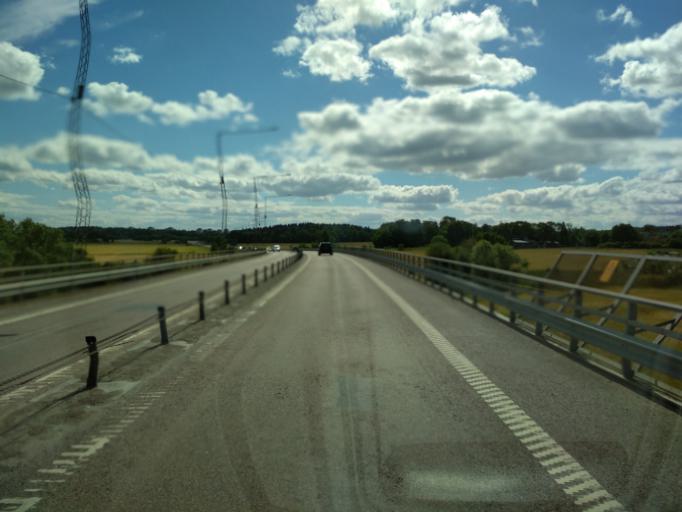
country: SE
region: Uppsala
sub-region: Uppsala Kommun
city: Uppsala
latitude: 59.8680
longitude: 17.5961
